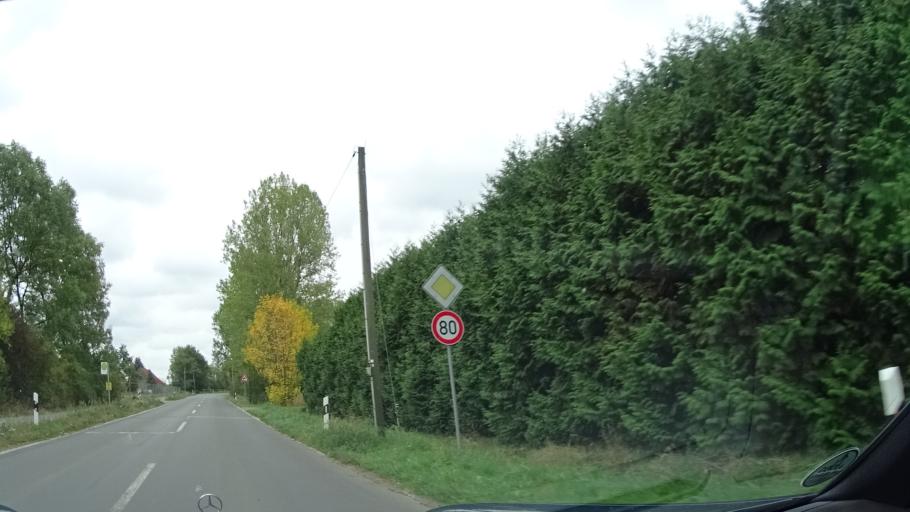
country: DE
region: Brandenburg
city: Dabergotz
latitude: 52.9233
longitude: 12.7564
